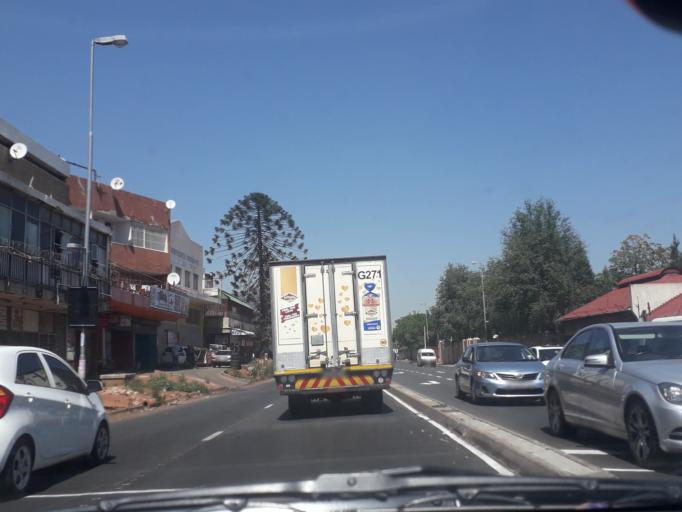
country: ZA
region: Gauteng
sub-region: City of Johannesburg Metropolitan Municipality
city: Johannesburg
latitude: -26.1763
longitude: 28.0646
